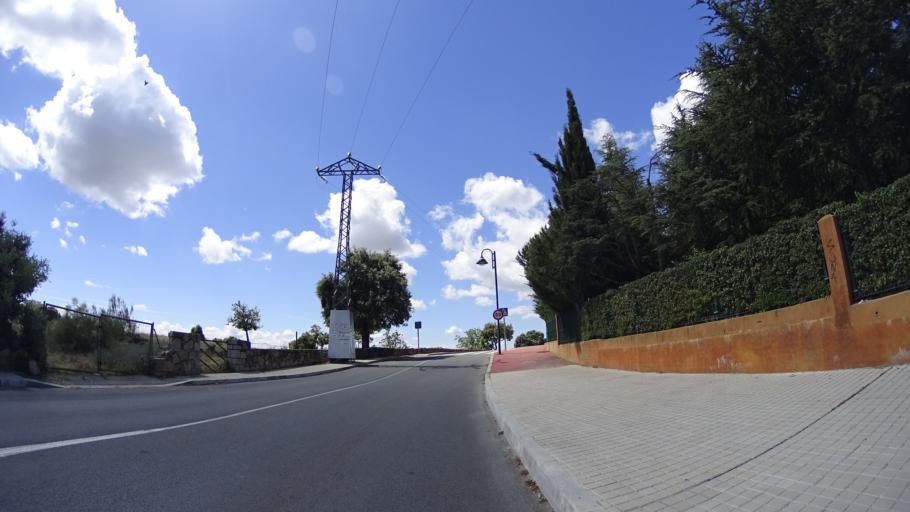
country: ES
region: Madrid
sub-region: Provincia de Madrid
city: Galapagar
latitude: 40.5700
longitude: -4.0077
